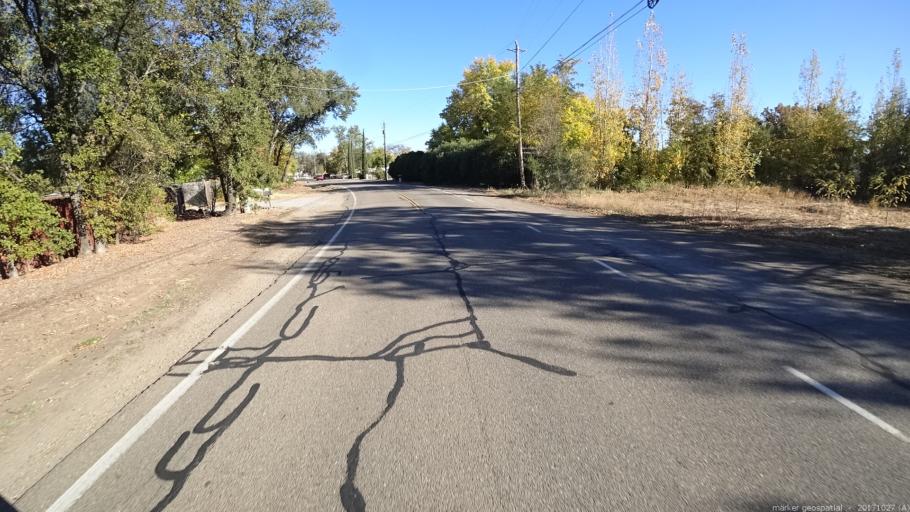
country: US
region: California
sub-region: Shasta County
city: Palo Cedro
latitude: 40.5493
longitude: -122.1786
